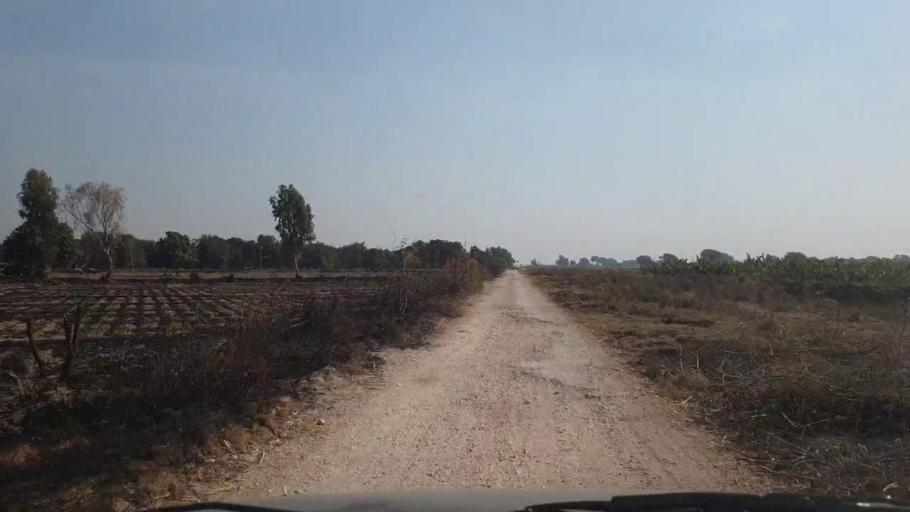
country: PK
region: Sindh
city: Chambar
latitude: 25.3594
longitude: 68.8023
